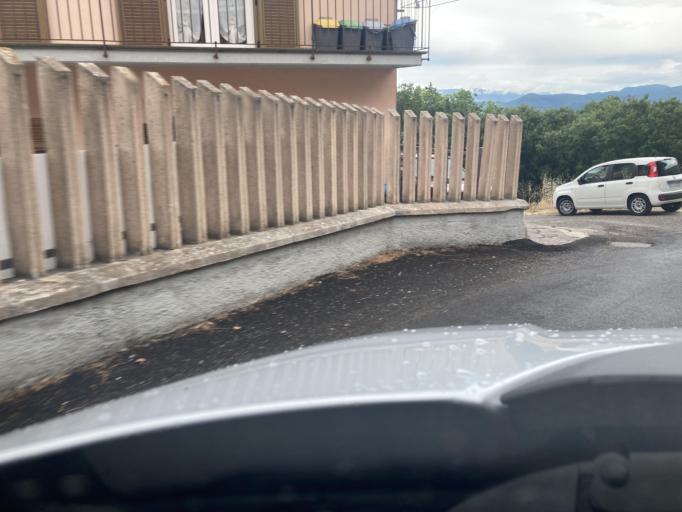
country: IT
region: Abruzzo
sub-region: Provincia dell' Aquila
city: San Panfilo d'Ocre
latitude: 42.2846
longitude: 13.4760
